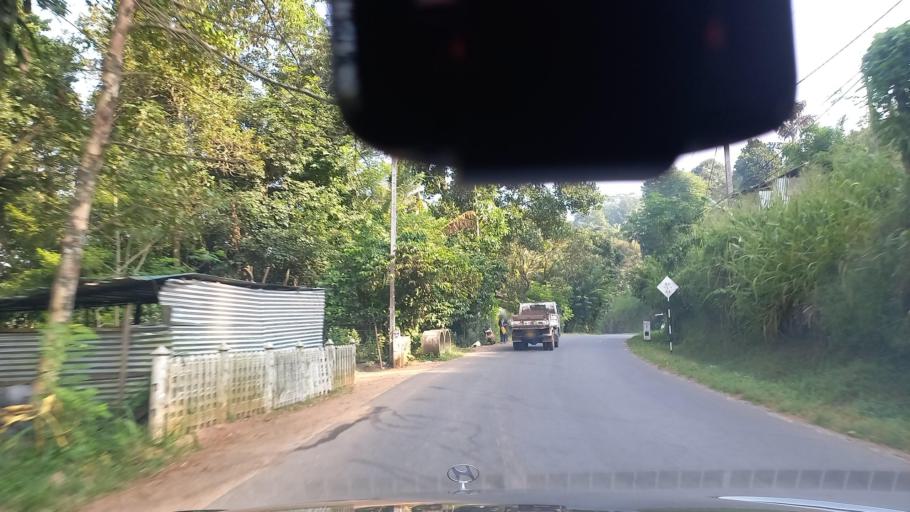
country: LK
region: Central
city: Kandy
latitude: 7.2303
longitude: 80.6032
